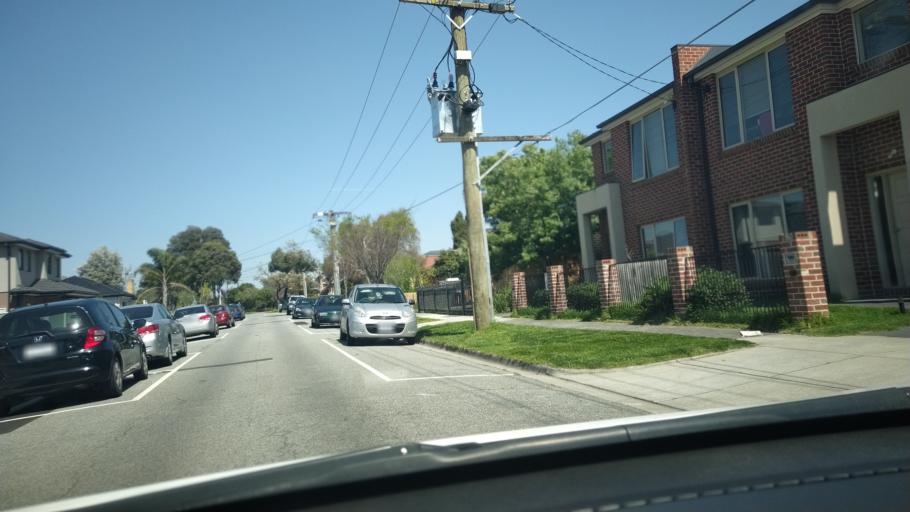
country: AU
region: Victoria
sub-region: Greater Dandenong
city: Noble Park
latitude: -37.9698
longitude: 145.1769
